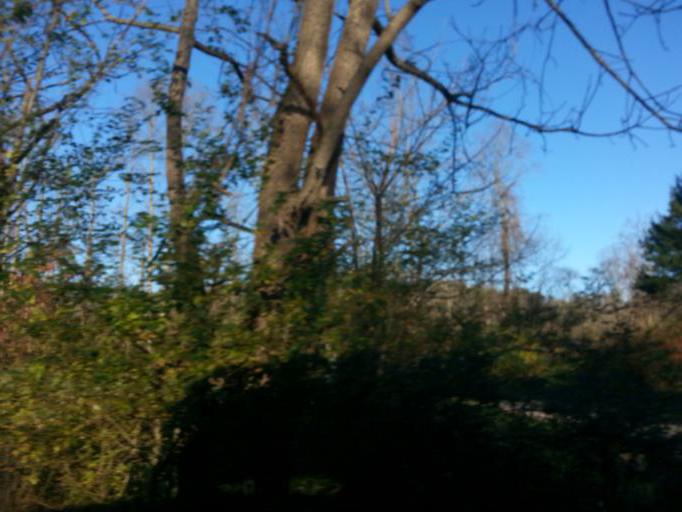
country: US
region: Tennessee
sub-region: Anderson County
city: Oak Ridge
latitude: 36.0905
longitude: -84.2389
